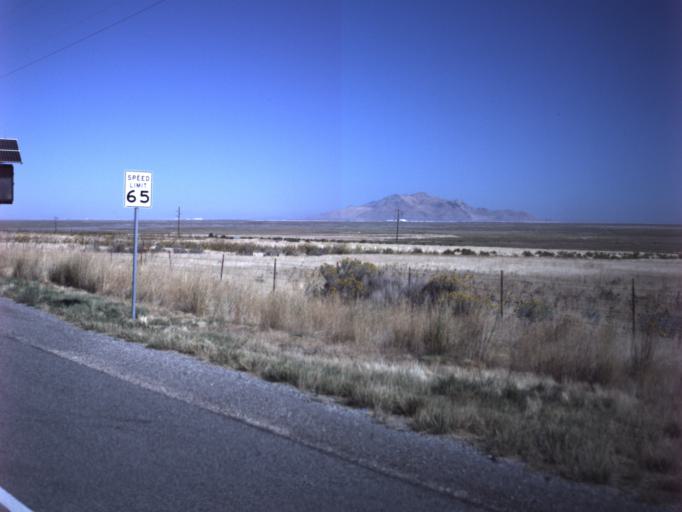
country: US
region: Utah
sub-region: Tooele County
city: Grantsville
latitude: 40.6290
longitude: -112.5116
